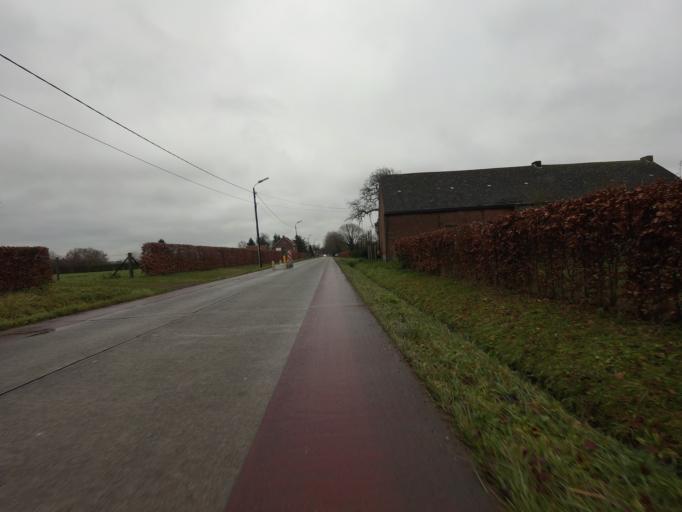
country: BE
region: Flanders
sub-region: Provincie Antwerpen
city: Sint-Katelijne-Waver
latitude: 51.0527
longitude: 4.5339
